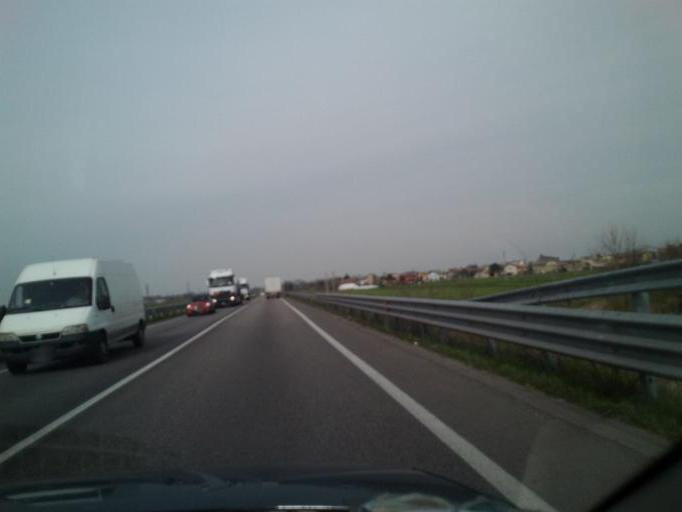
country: IT
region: Lombardy
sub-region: Provincia di Mantova
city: Marmirolo
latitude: 45.2120
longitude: 10.7554
